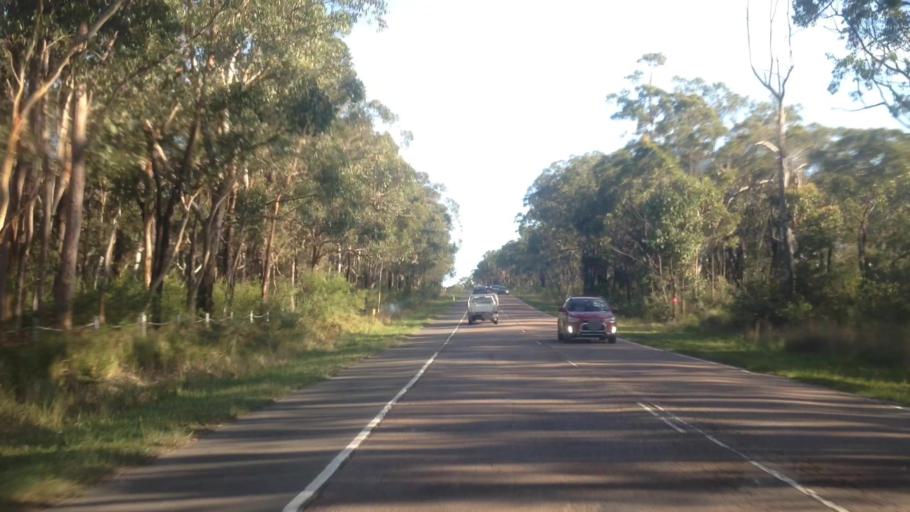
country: AU
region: New South Wales
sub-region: Lake Macquarie Shire
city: Dora Creek
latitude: -33.1398
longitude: 151.4777
